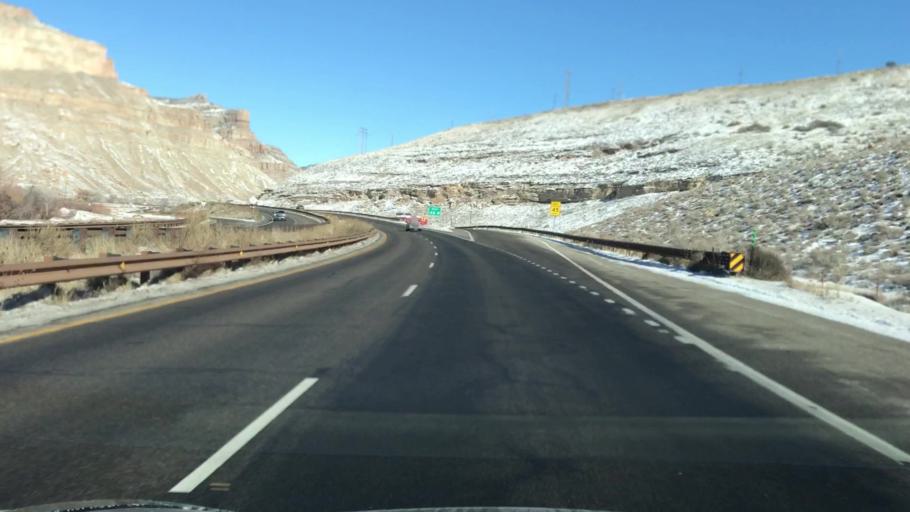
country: US
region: Colorado
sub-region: Mesa County
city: Palisade
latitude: 39.1400
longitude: -108.3161
